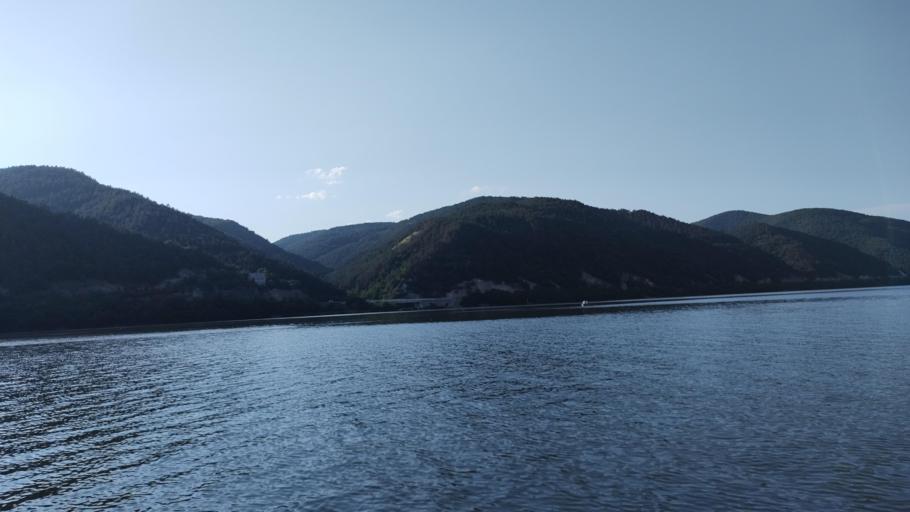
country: RO
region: Mehedinti
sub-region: Comuna Svinita
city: Svinita
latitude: 44.5248
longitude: 22.2080
